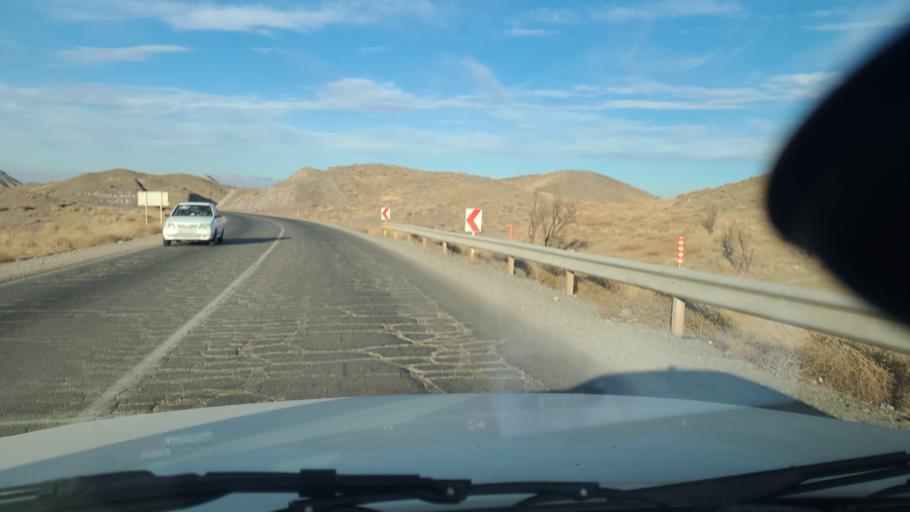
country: IR
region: Razavi Khorasan
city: Sabzevar
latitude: 36.4117
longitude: 57.5508
